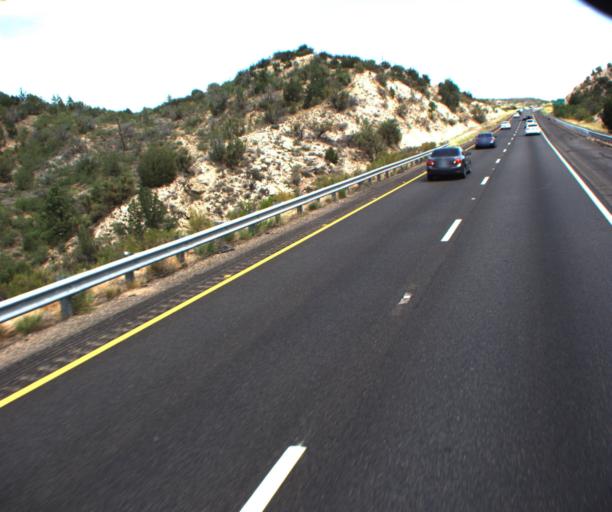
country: US
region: Arizona
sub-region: Yavapai County
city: Camp Verde
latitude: 34.5491
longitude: -111.9056
